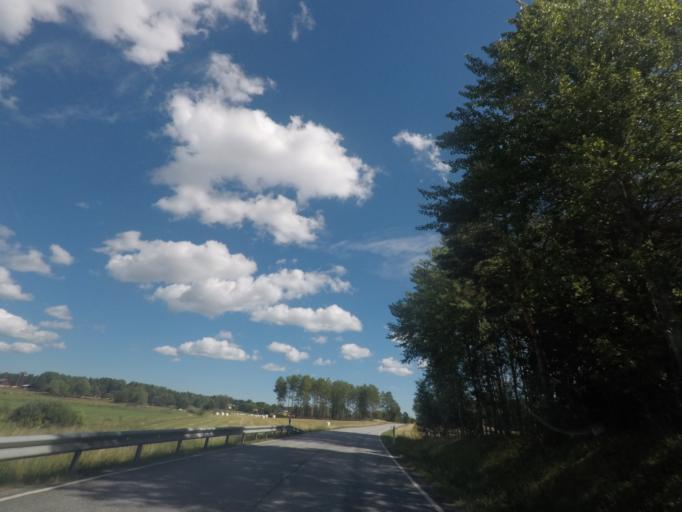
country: SE
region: Stockholm
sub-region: Norrtalje Kommun
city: Hallstavik
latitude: 59.9526
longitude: 18.7679
